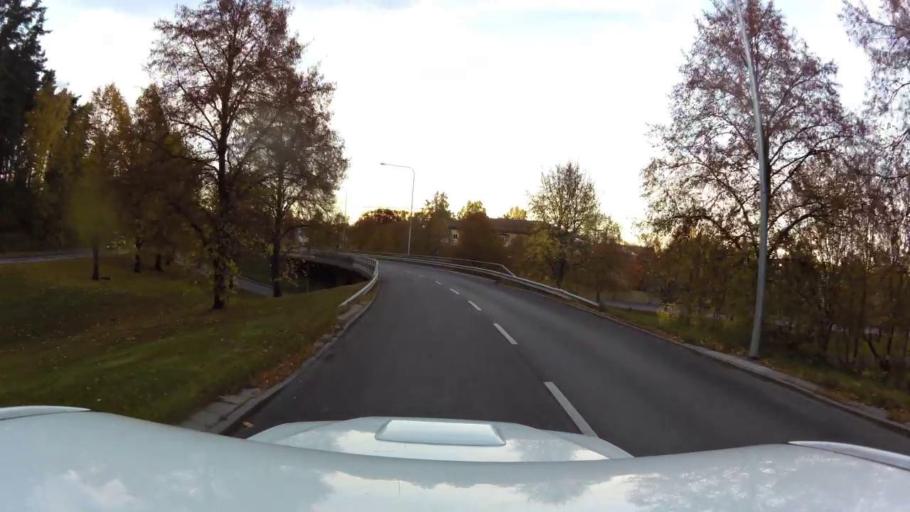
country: SE
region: OEstergoetland
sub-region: Linkopings Kommun
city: Linkoping
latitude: 58.4009
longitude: 15.6365
